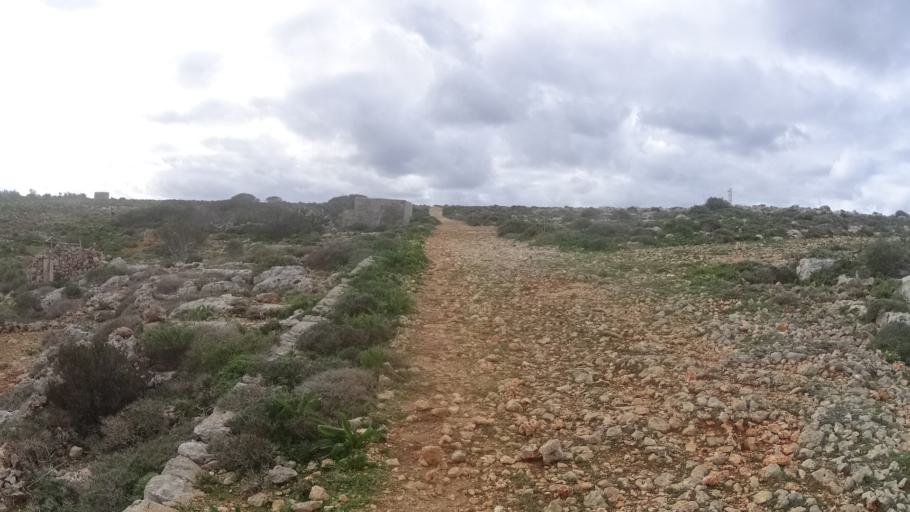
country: MT
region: Il-Mellieha
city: Mellieha
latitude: 35.9746
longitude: 14.3264
